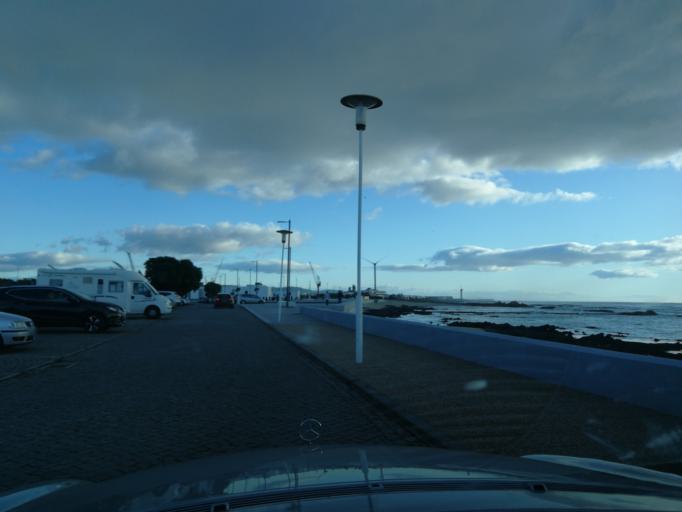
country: PT
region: Viana do Castelo
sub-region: Viana do Castelo
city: Viana do Castelo
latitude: 41.6983
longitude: -8.8520
